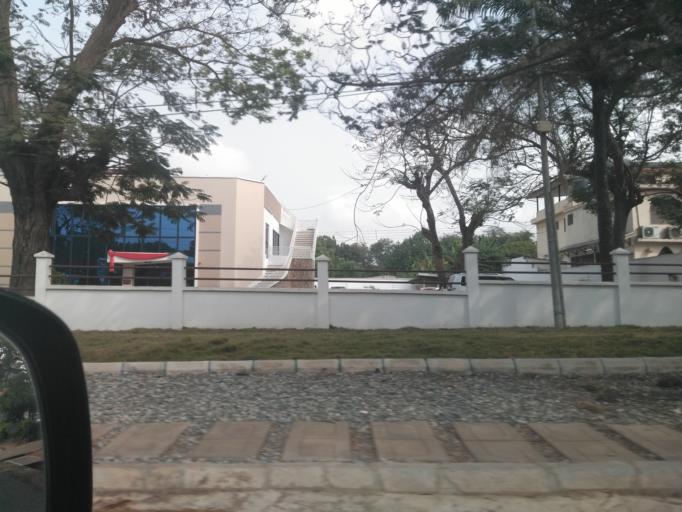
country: GH
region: Greater Accra
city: Accra
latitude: 5.6096
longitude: -0.1820
